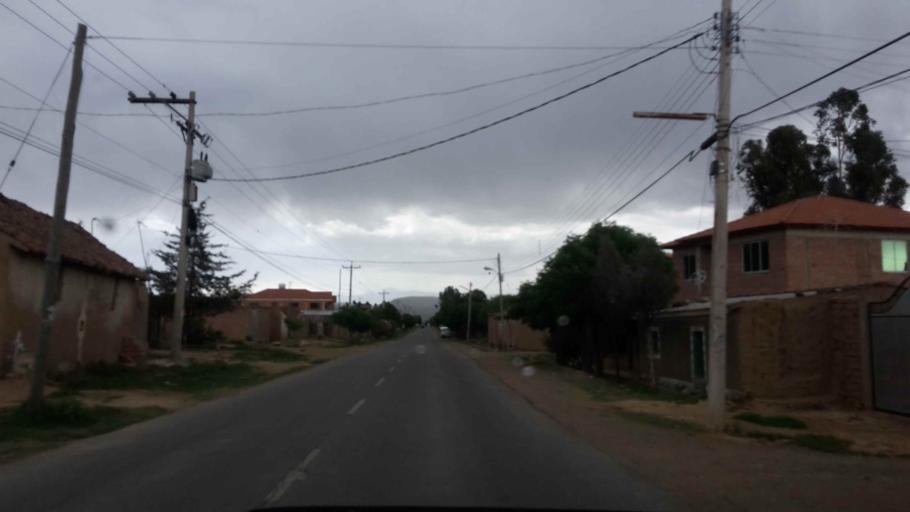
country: BO
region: Cochabamba
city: Tarata
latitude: -17.5862
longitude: -66.0506
